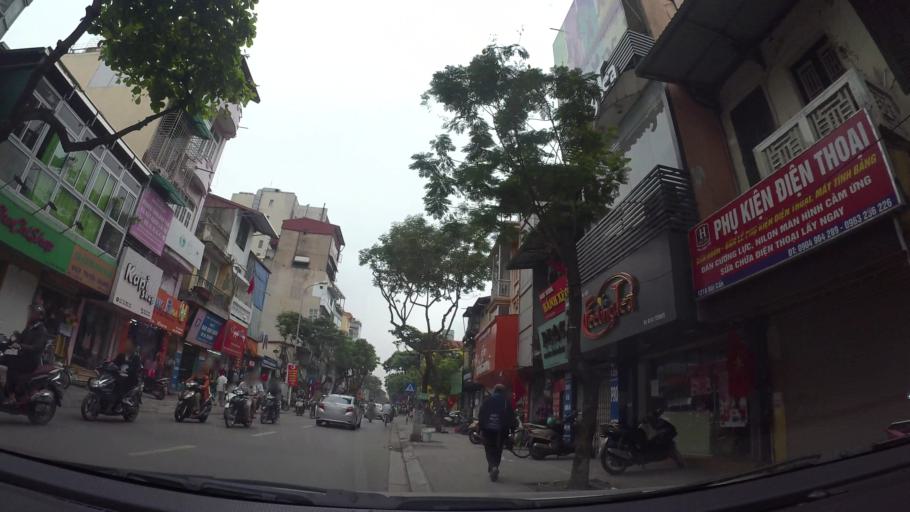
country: VN
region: Ha Noi
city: Dong Da
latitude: 21.0348
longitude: 105.8285
